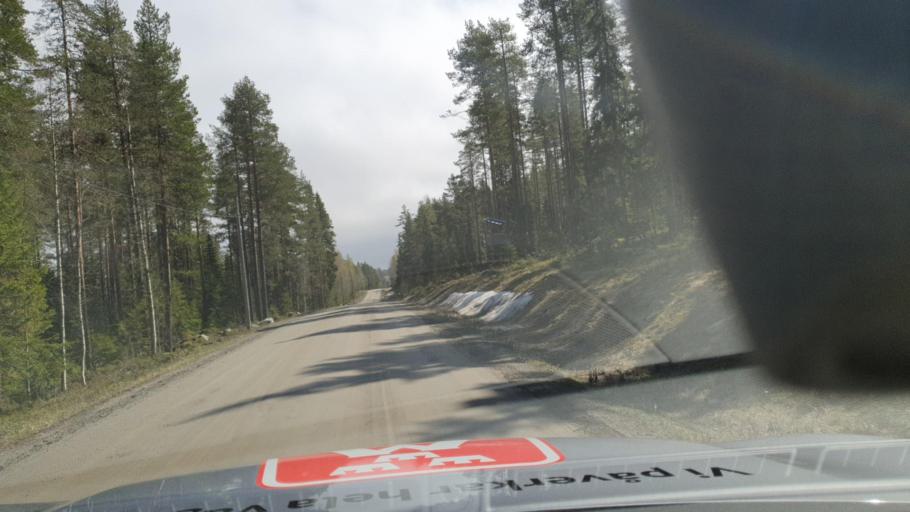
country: SE
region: Vaesterbotten
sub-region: Bjurholms Kommun
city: Bjurholm
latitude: 63.6782
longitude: 18.9893
